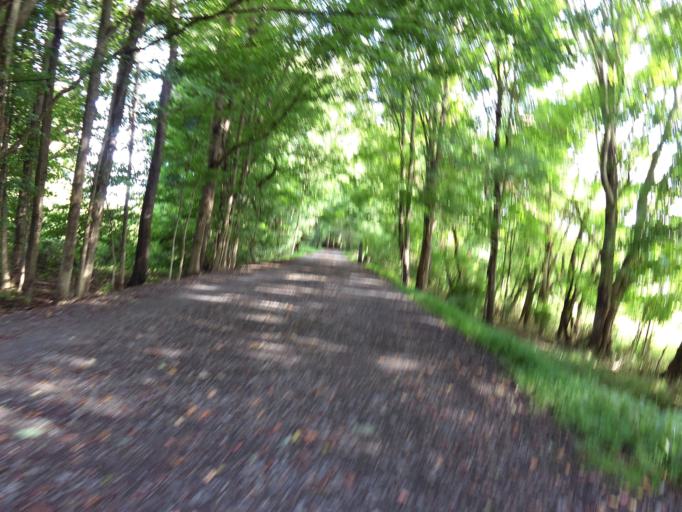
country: US
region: Virginia
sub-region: Washington County
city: Abingdon
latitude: 36.7047
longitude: -81.9654
